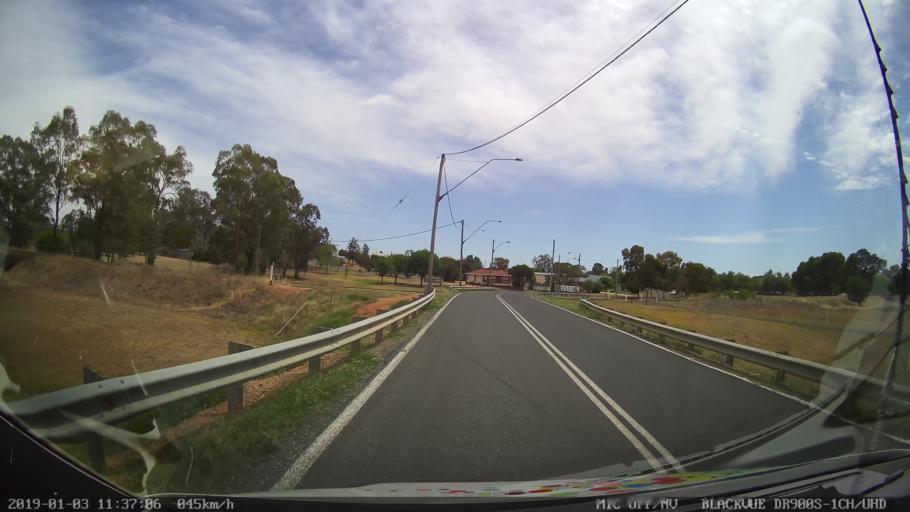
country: AU
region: New South Wales
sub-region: Weddin
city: Grenfell
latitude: -33.9050
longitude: 148.1604
